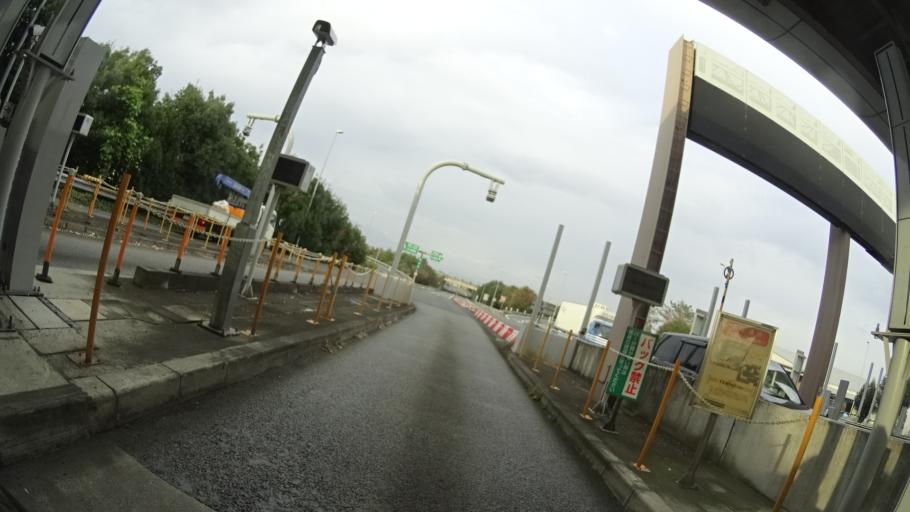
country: JP
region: Gunma
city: Isesaki
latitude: 36.3528
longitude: 139.2197
